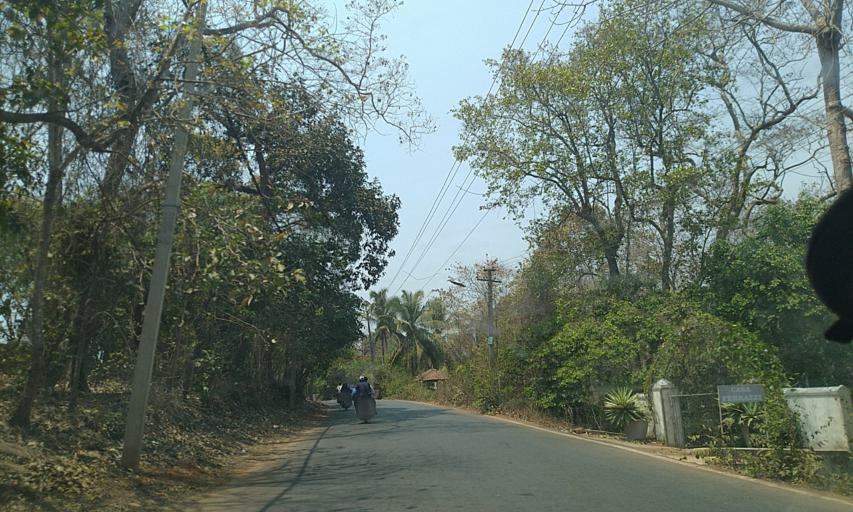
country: IN
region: Goa
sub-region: North Goa
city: Solim
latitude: 15.5975
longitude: 73.7826
